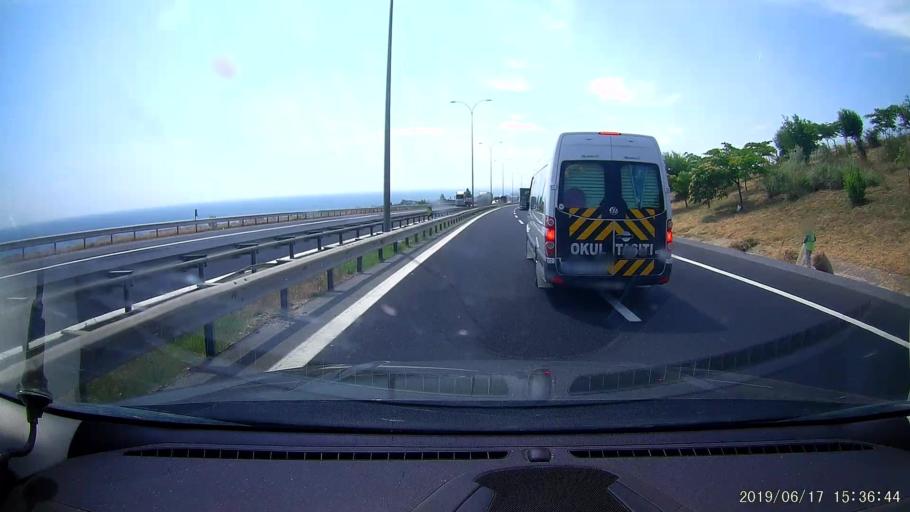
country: TR
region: Istanbul
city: Celaliye
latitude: 41.0508
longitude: 28.4424
